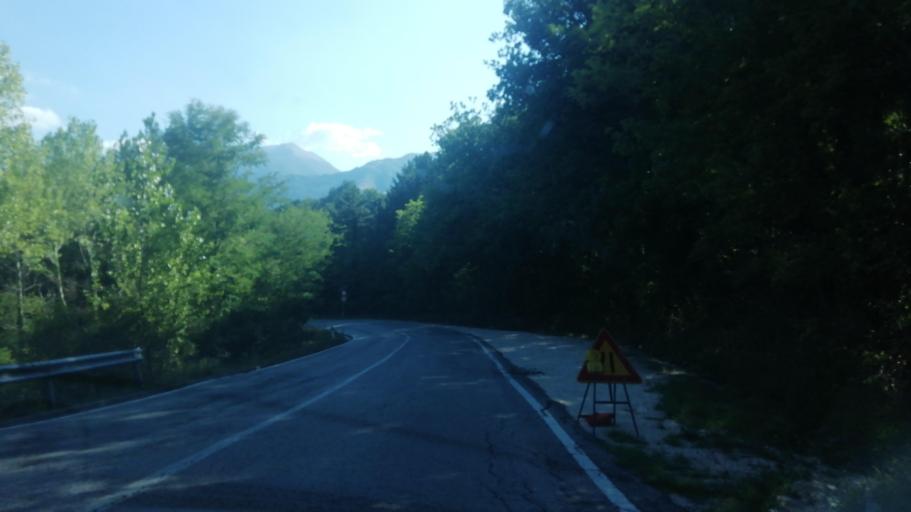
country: IT
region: The Marches
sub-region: Provincia di Pesaro e Urbino
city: Cagli
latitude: 43.5423
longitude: 12.6992
